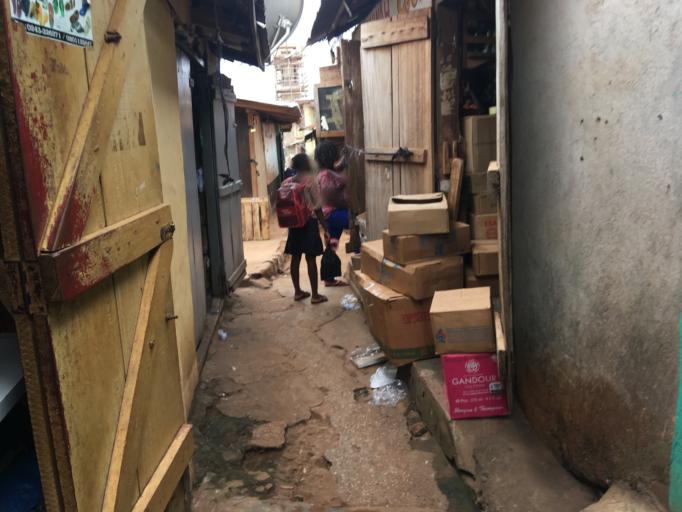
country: GH
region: Western
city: Bibiani
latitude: 6.8039
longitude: -2.5161
